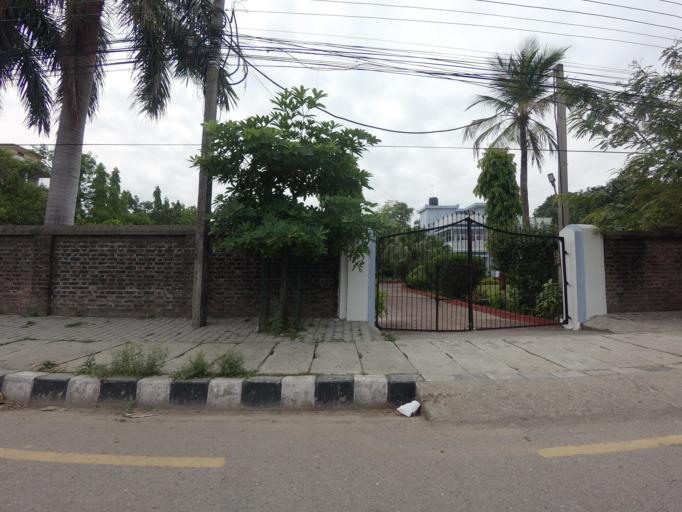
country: NP
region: Western Region
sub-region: Lumbini Zone
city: Bhairahawa
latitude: 27.4957
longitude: 83.4467
